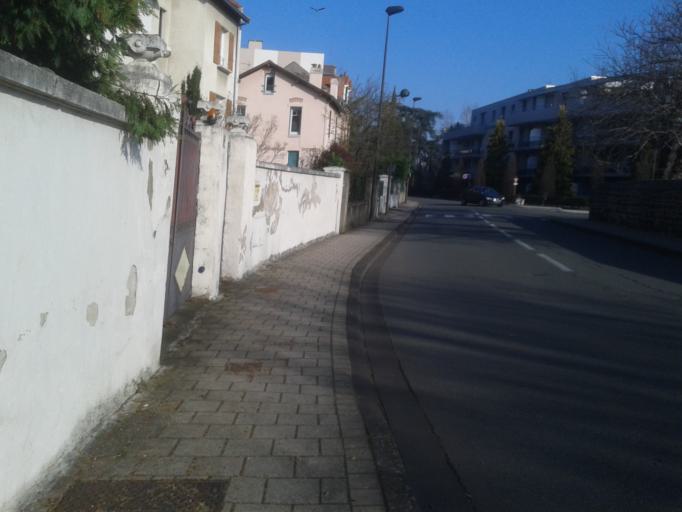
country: FR
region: Auvergne
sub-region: Departement du Puy-de-Dome
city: Chamalieres
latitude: 45.7709
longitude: 3.0684
